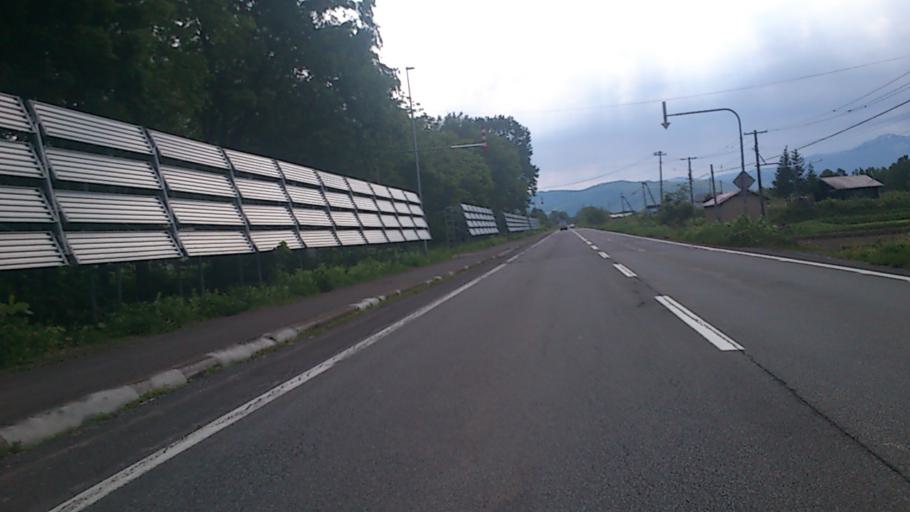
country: JP
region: Hokkaido
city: Kamikawa
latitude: 43.8492
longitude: 142.7345
